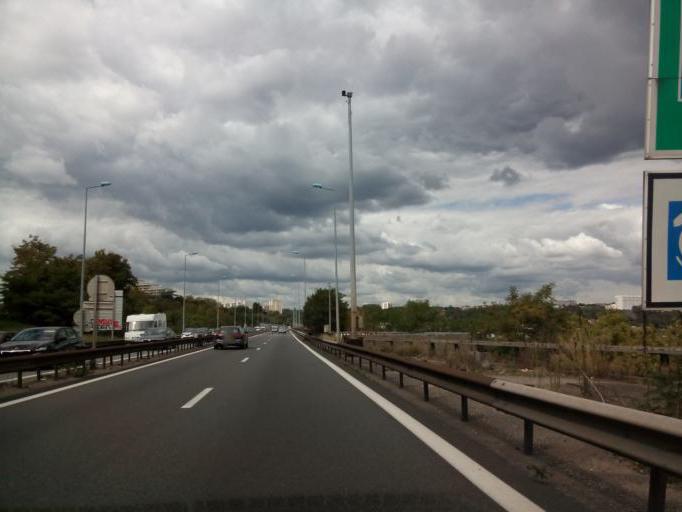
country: FR
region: Rhone-Alpes
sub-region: Departement du Rhone
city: Tassin-la-Demi-Lune
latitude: 45.7656
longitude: 4.7997
